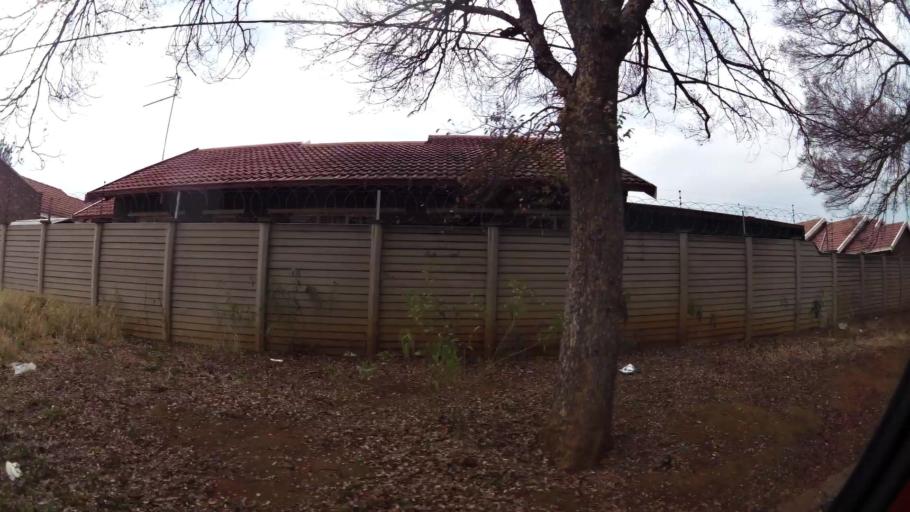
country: ZA
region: Gauteng
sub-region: Sedibeng District Municipality
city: Vanderbijlpark
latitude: -26.7015
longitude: 27.8423
